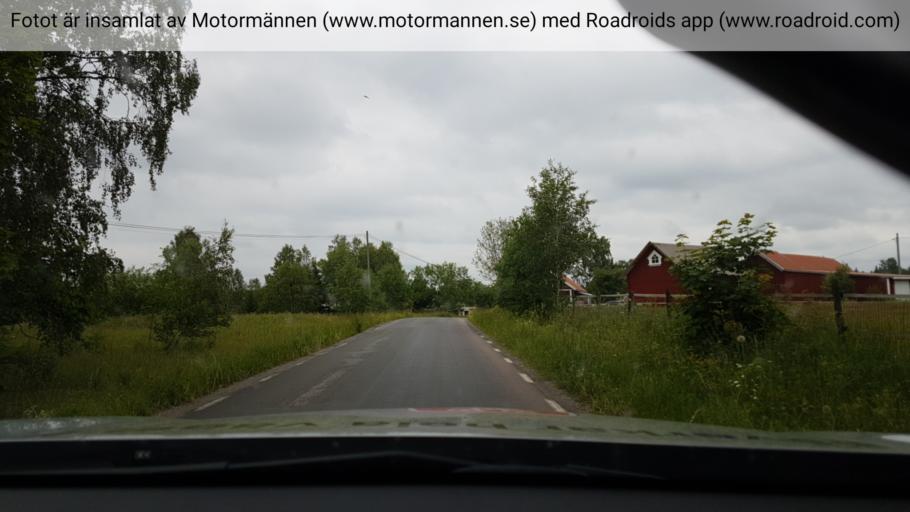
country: SE
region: Vaestra Goetaland
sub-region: Skovde Kommun
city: Skultorp
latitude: 58.2886
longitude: 13.8197
